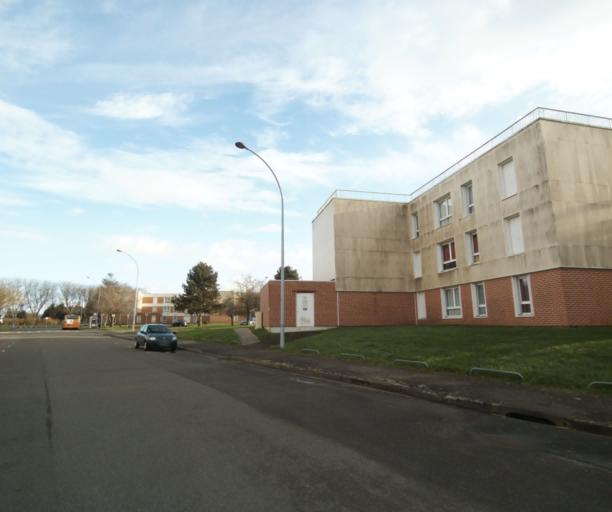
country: FR
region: Pays de la Loire
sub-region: Departement de la Sarthe
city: Le Mans
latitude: 47.9637
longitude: 0.2072
